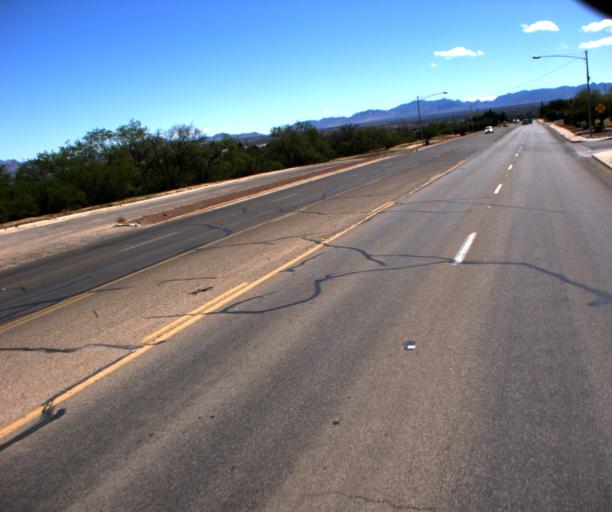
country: US
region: Arizona
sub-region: Cochise County
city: Benson
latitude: 31.9702
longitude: -110.3060
